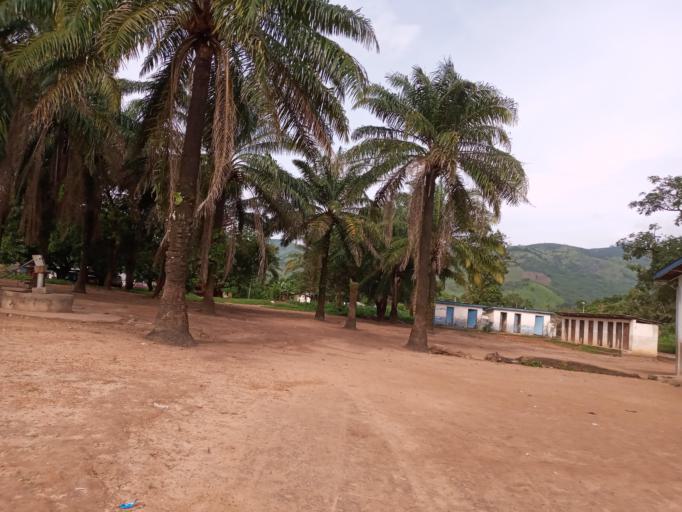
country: SL
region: Northern Province
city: Bumbuna
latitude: 9.0459
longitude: -11.7523
